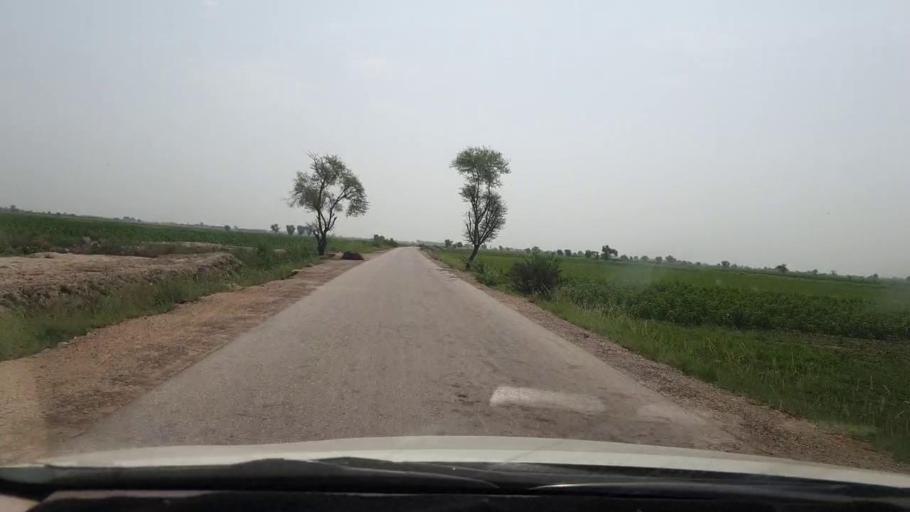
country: PK
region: Sindh
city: Rohri
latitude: 27.5381
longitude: 68.9982
